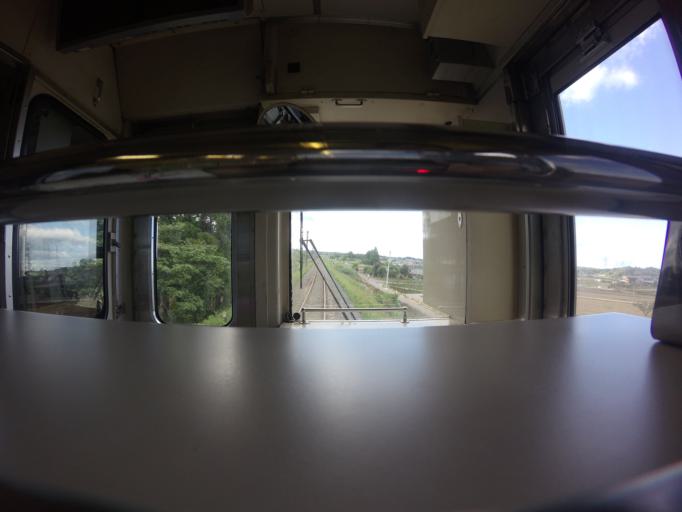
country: JP
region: Fukushima
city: Namie
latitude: 37.5879
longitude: 141.0018
